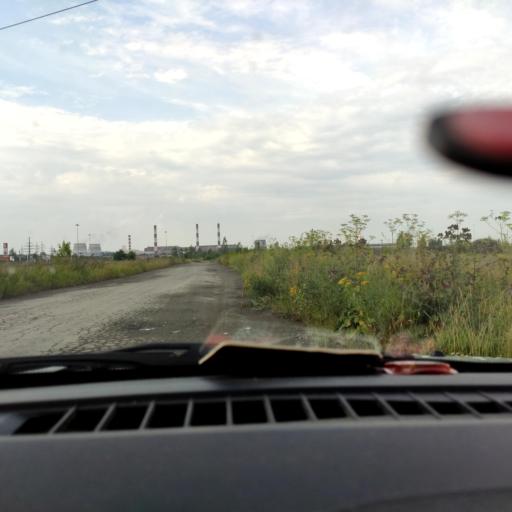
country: RU
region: Perm
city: Kondratovo
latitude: 57.9399
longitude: 56.1596
